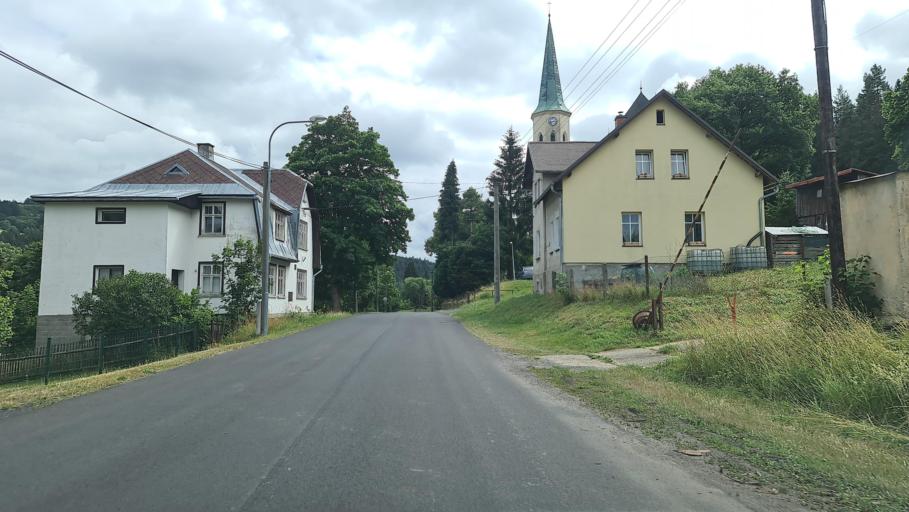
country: CZ
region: Karlovarsky
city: Kraslice
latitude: 50.3605
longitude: 12.5242
